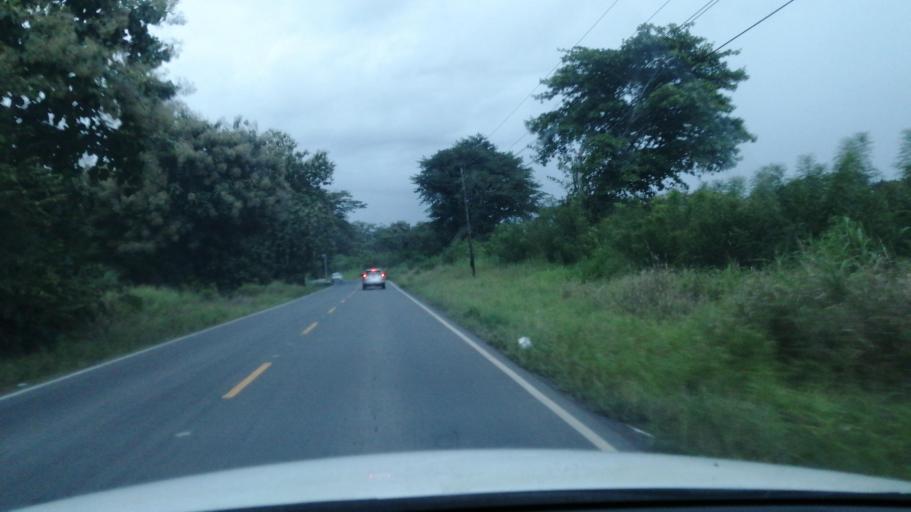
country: PA
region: Chiriqui
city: Alanje
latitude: 8.3954
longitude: -82.4929
